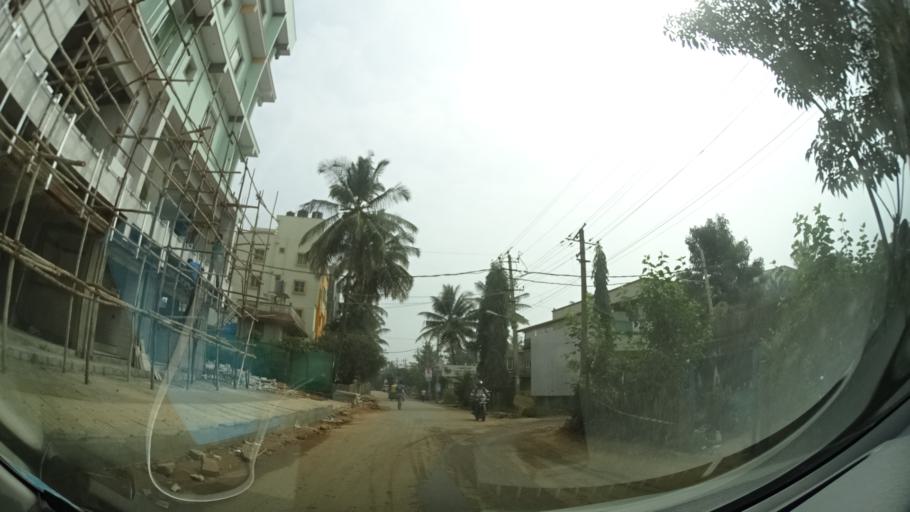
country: IN
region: Karnataka
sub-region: Bangalore Rural
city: Hoskote
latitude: 12.9652
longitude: 77.7566
